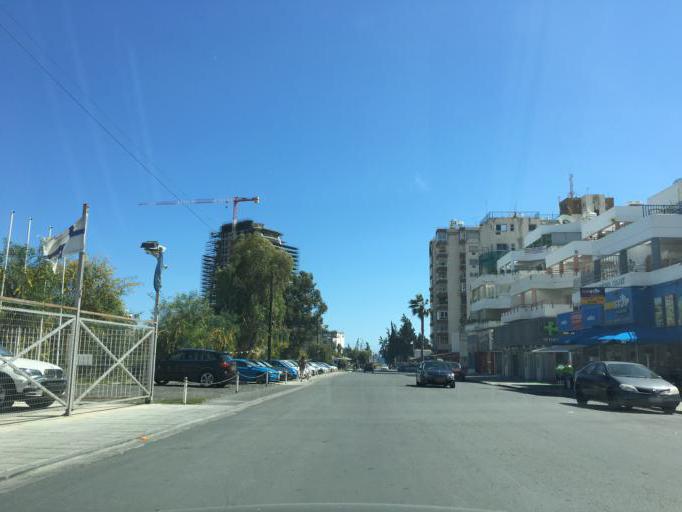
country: CY
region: Limassol
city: Limassol
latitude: 34.6919
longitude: 33.0681
